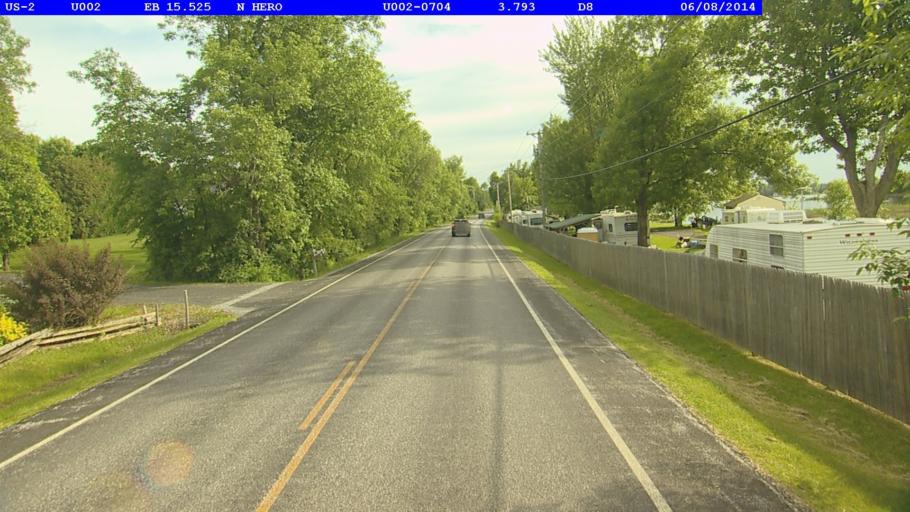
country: US
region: Vermont
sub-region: Grand Isle County
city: North Hero
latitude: 44.8377
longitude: -73.2705
